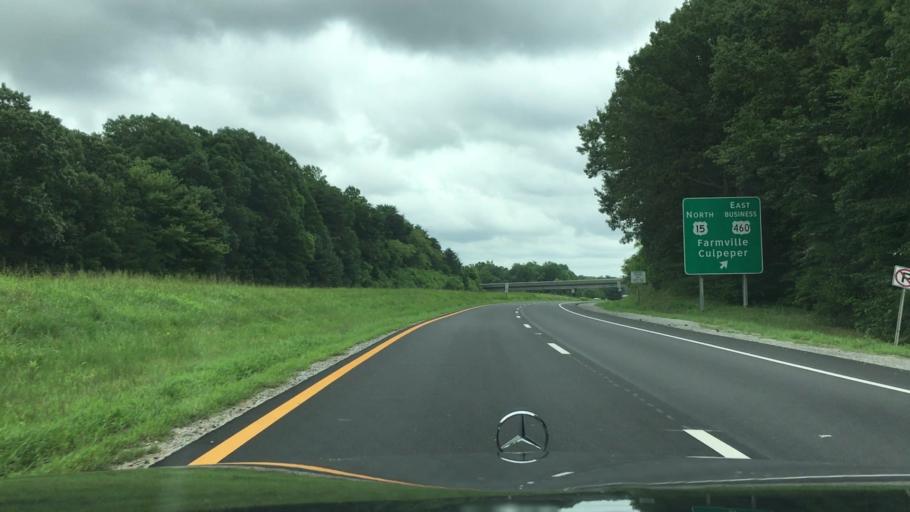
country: US
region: Virginia
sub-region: Prince Edward County
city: Hampden Sydney
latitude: 37.3157
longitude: -78.4696
